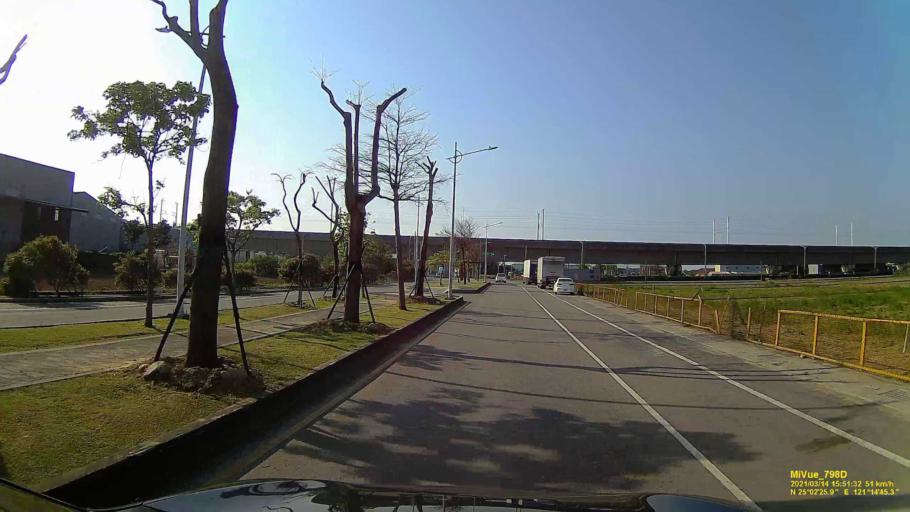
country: TW
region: Taiwan
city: Taoyuan City
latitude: 25.0407
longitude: 121.2457
